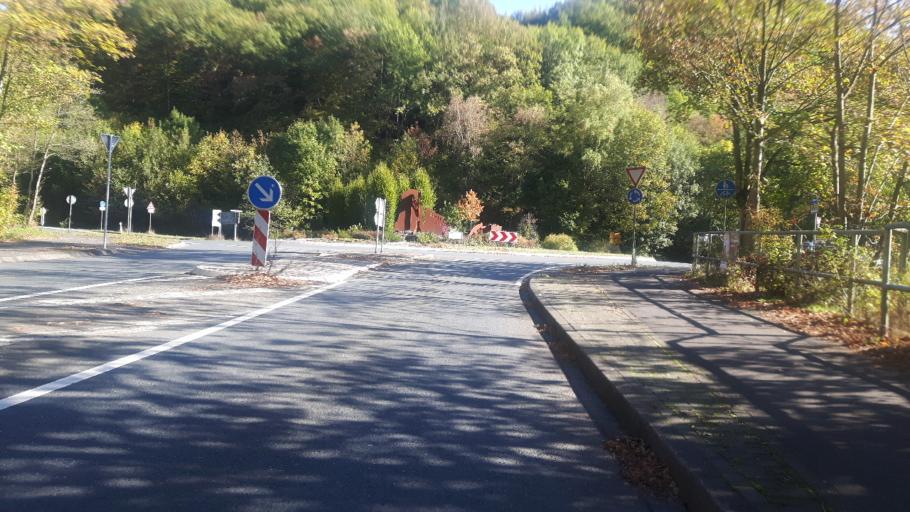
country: DE
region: Rheinland-Pfalz
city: Niederirsen
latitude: 50.8119
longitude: 7.6025
